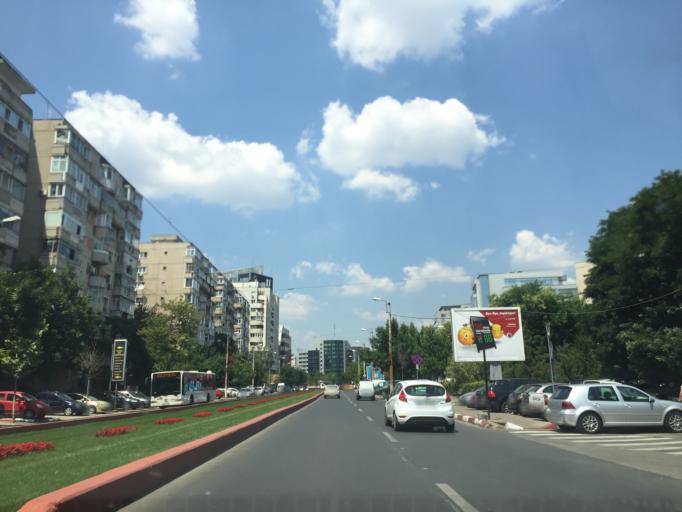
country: RO
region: Bucuresti
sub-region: Municipiul Bucuresti
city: Bucharest
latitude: 44.4209
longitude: 26.1252
